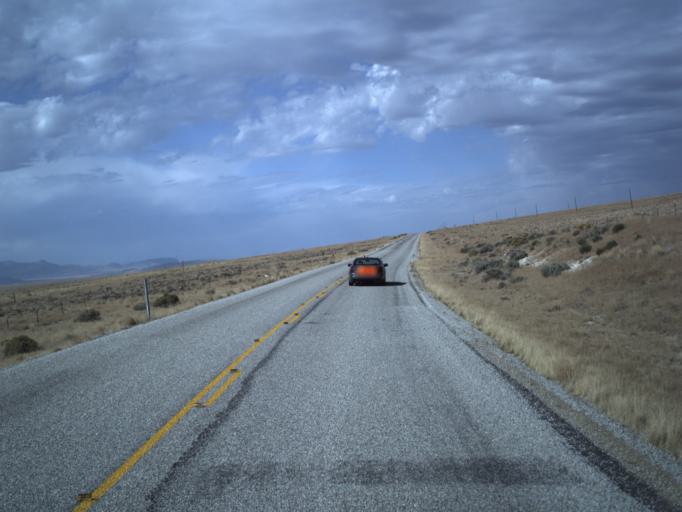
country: US
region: Utah
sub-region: Tooele County
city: Wendover
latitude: 41.4419
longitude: -113.6947
